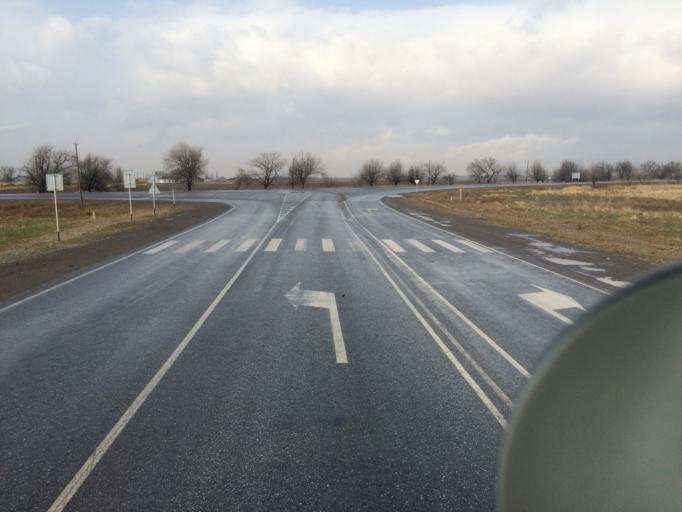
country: KZ
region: Zhambyl
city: Georgiyevka
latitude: 43.0883
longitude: 74.7067
